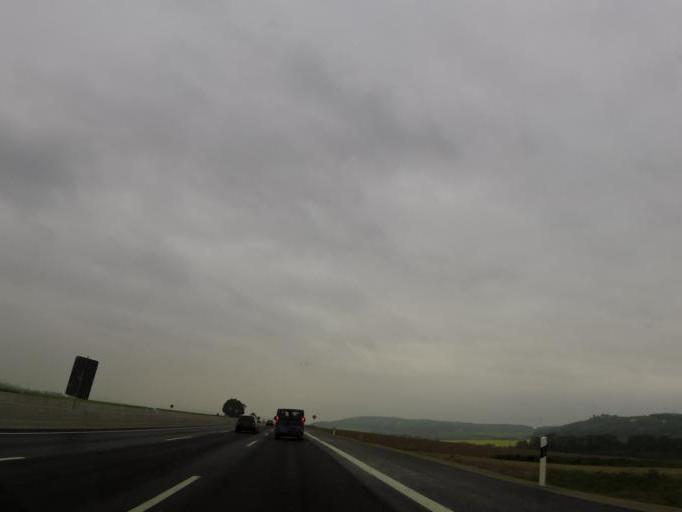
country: DE
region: Lower Saxony
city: Seesen
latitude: 51.9097
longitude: 10.1340
